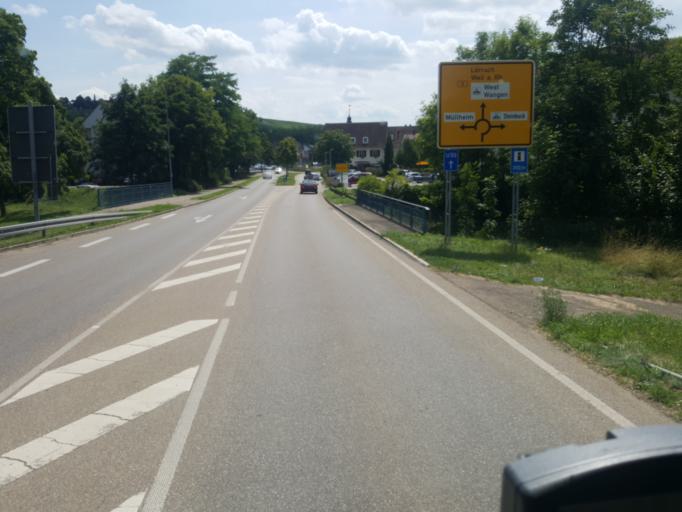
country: DE
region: Baden-Wuerttemberg
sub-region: Freiburg Region
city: Mullheim
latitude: 47.8142
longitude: 7.6110
